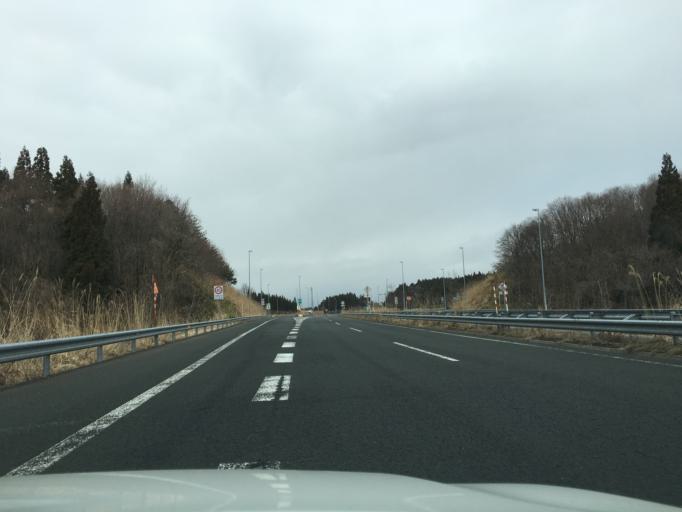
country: JP
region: Akita
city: Tenno
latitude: 40.0067
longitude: 140.0884
